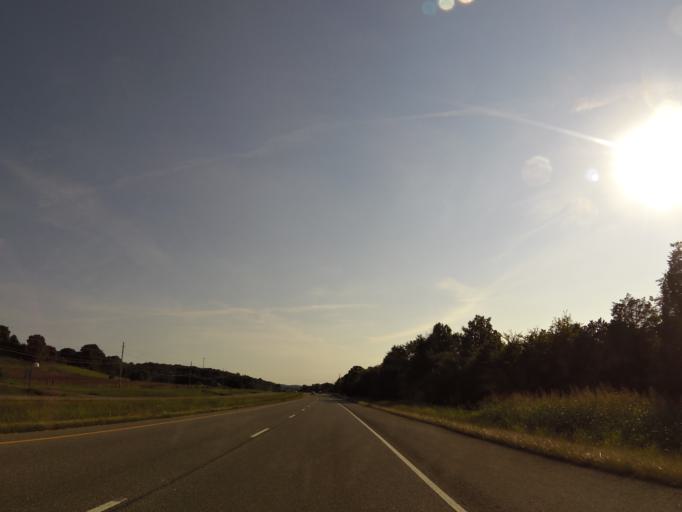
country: US
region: Tennessee
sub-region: Loudon County
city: Greenback
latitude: 35.6222
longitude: -84.1890
